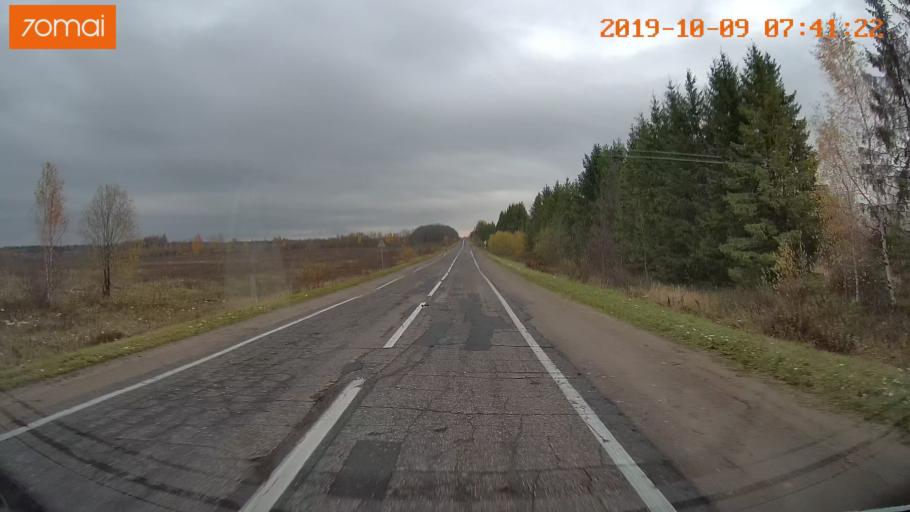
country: RU
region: Jaroslavl
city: Kukoboy
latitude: 58.6385
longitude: 39.7058
